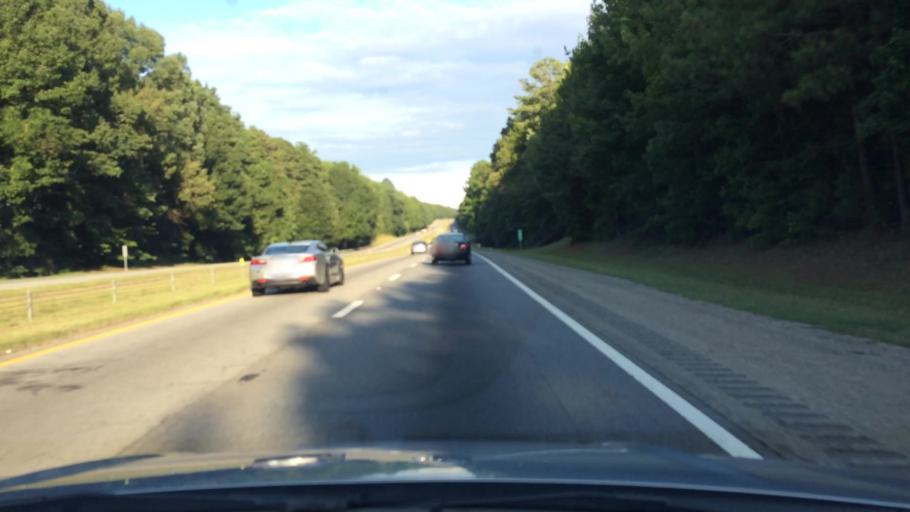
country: US
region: South Carolina
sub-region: Lexington County
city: Chapin
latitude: 34.2105
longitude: -81.3858
